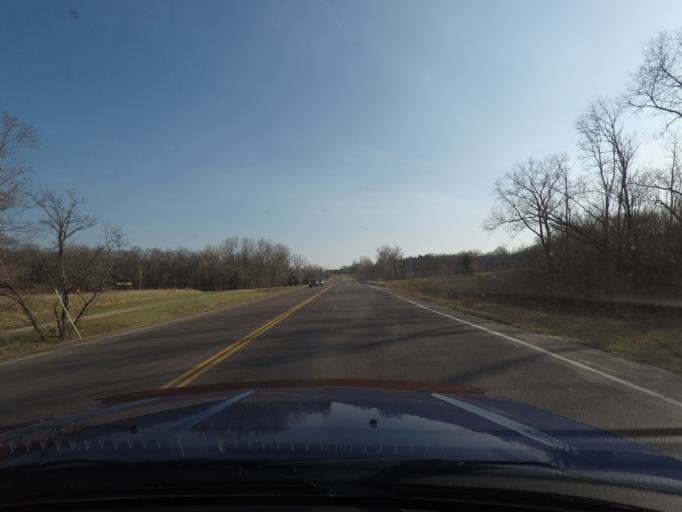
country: US
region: Kansas
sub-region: Douglas County
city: Lawrence
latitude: 39.0454
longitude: -95.3898
